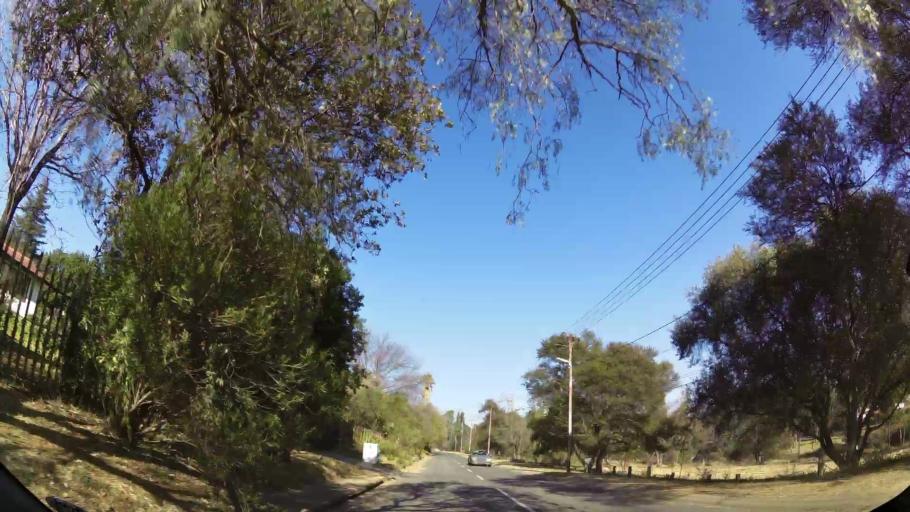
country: ZA
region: Gauteng
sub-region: City of Johannesburg Metropolitan Municipality
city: Midrand
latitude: -26.0696
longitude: 28.0399
